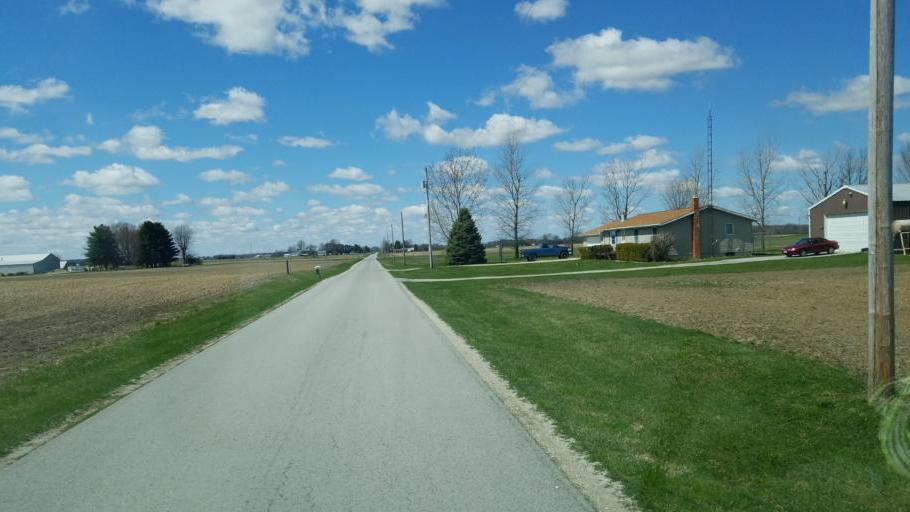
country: US
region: Ohio
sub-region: Seneca County
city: Fostoria
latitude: 41.0941
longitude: -83.5128
